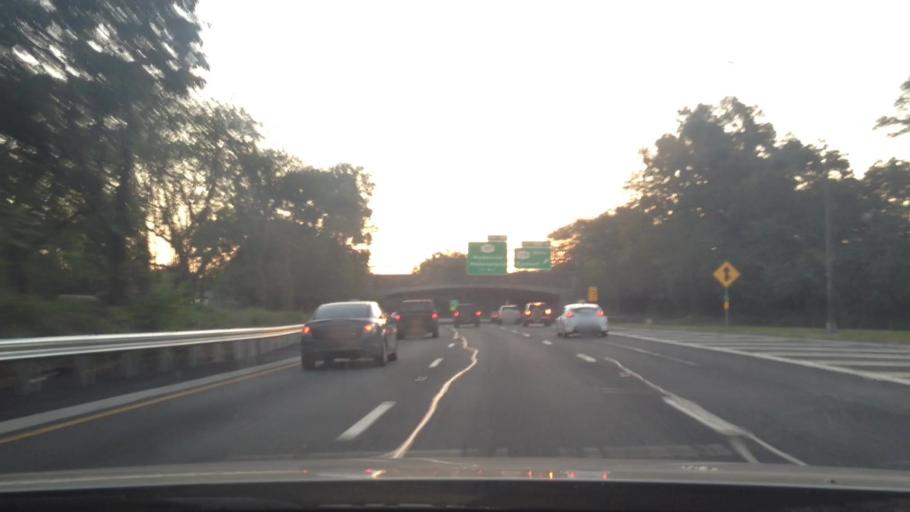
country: US
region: New York
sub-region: Nassau County
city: North Wantagh
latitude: 40.7010
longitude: -73.4919
